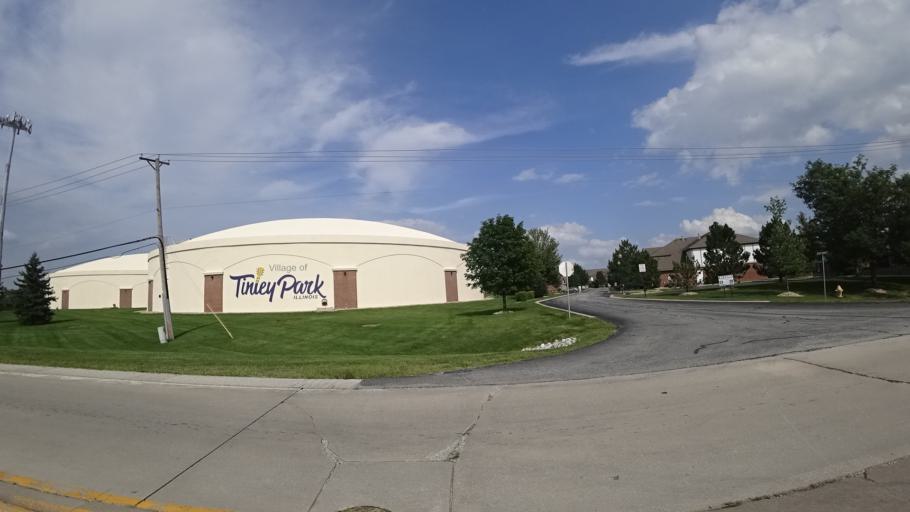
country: US
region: Illinois
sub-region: Cook County
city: Tinley Park
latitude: 41.5575
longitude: -87.7715
